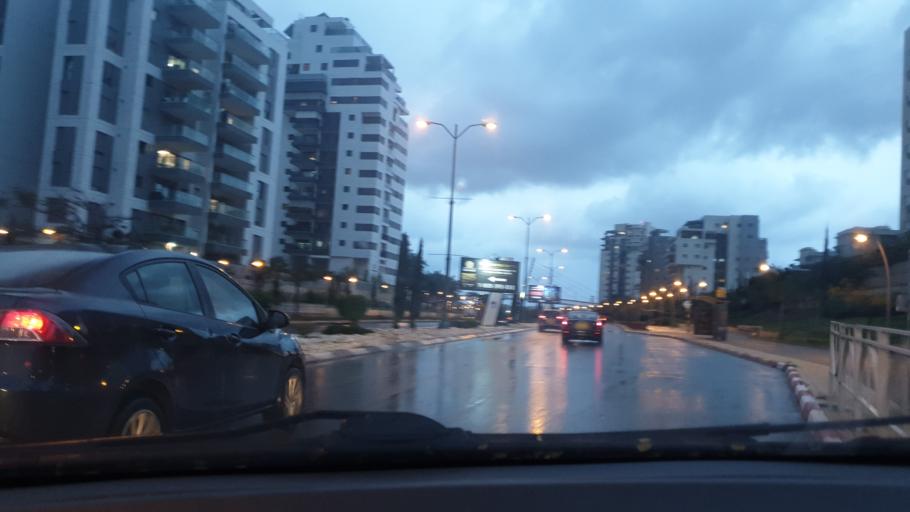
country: IL
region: Central District
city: Rishon LeZiyyon
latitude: 31.9816
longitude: 34.8069
